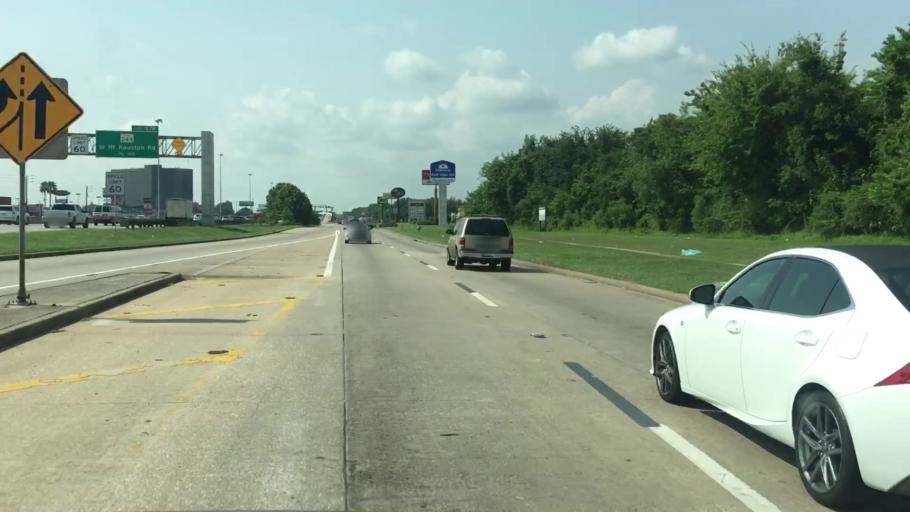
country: US
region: Texas
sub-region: Harris County
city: Aldine
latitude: 29.9286
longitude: -95.4110
